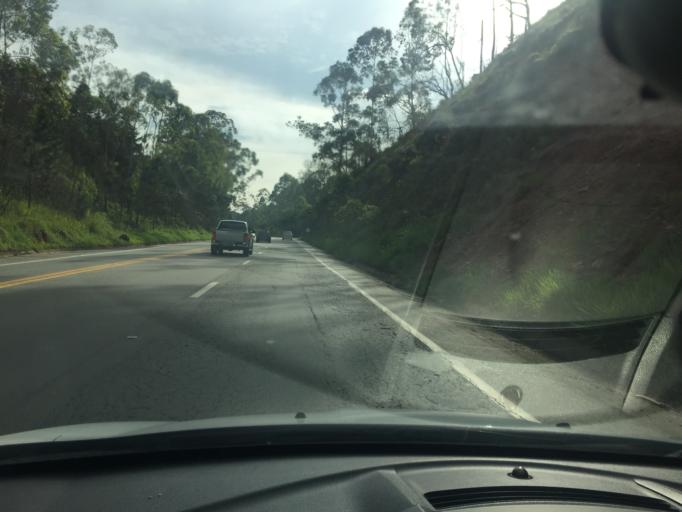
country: BR
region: Sao Paulo
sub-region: Campo Limpo Paulista
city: Campo Limpo Paulista
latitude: -23.1695
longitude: -46.7655
